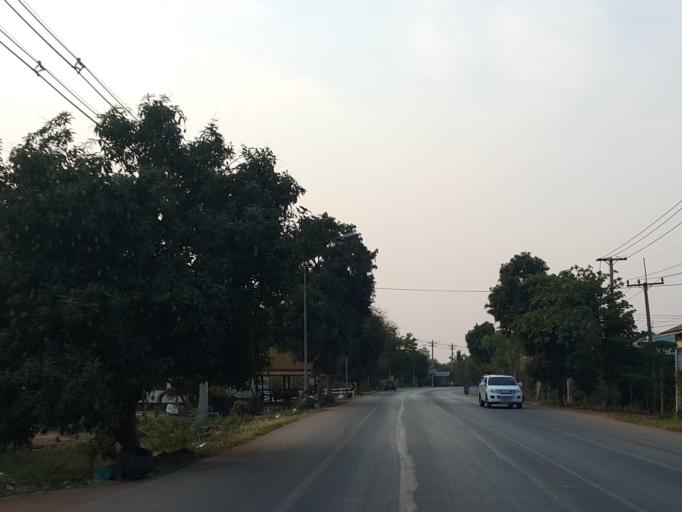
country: TH
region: Sukhothai
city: Si Samrong
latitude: 17.2270
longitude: 99.8592
